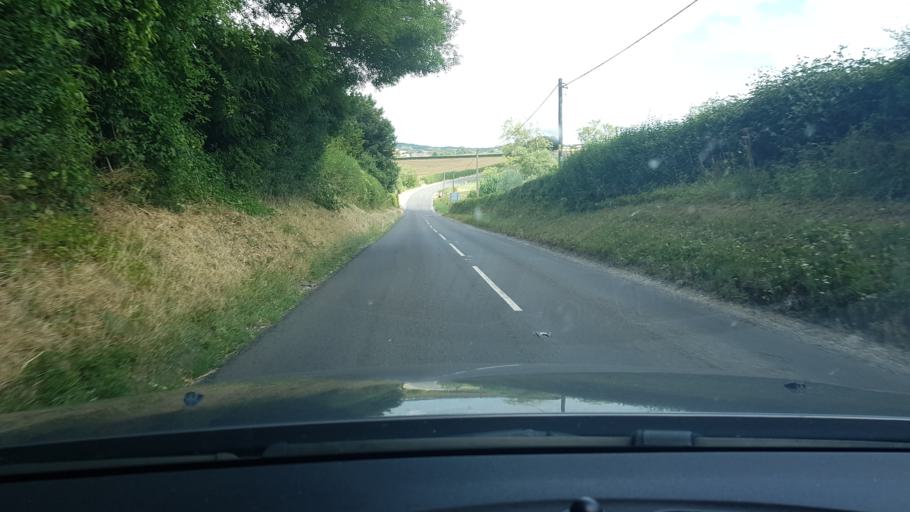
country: GB
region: England
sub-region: Wiltshire
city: Shalbourne
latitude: 51.3739
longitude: -1.5469
